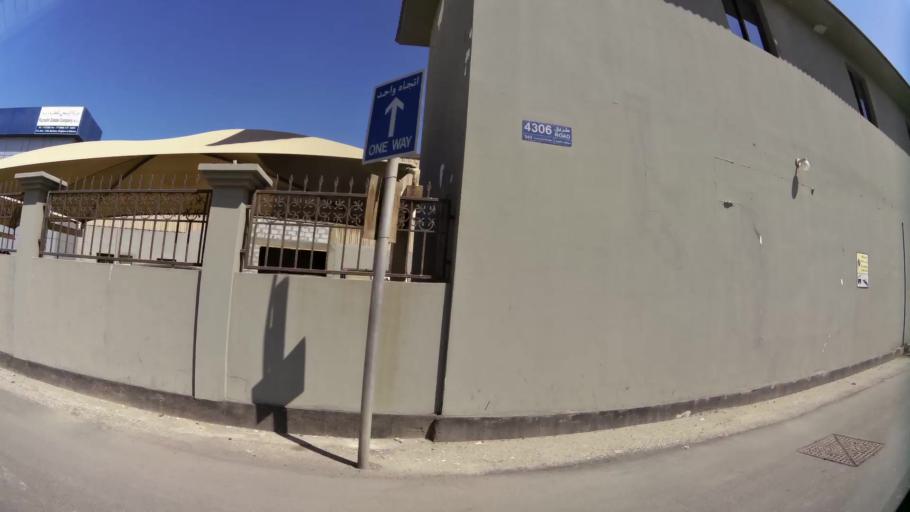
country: BH
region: Manama
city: Manama
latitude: 26.2012
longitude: 50.6010
